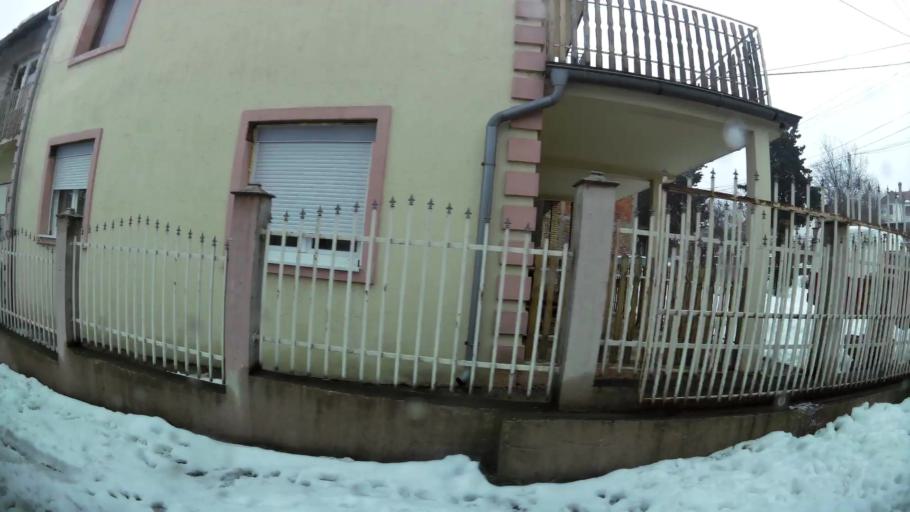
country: RS
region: Central Serbia
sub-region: Belgrade
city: Zvezdara
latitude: 44.7733
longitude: 20.5278
